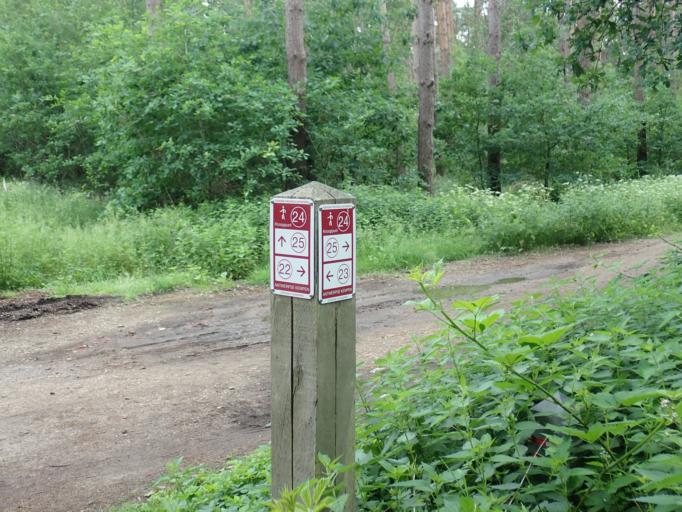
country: BE
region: Flanders
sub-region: Provincie Antwerpen
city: Lille
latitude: 51.2251
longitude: 4.8936
